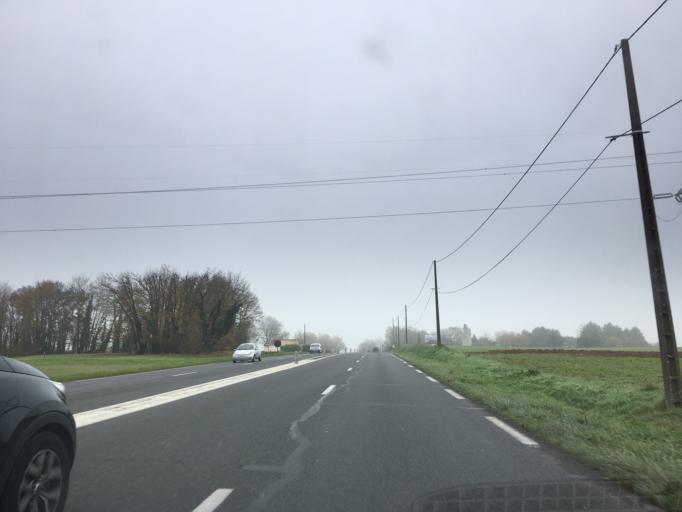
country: FR
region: Ile-de-France
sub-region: Departement de Seine-et-Marne
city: Vernou-la-Celle-sur-Seine
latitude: 48.3627
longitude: 2.8600
